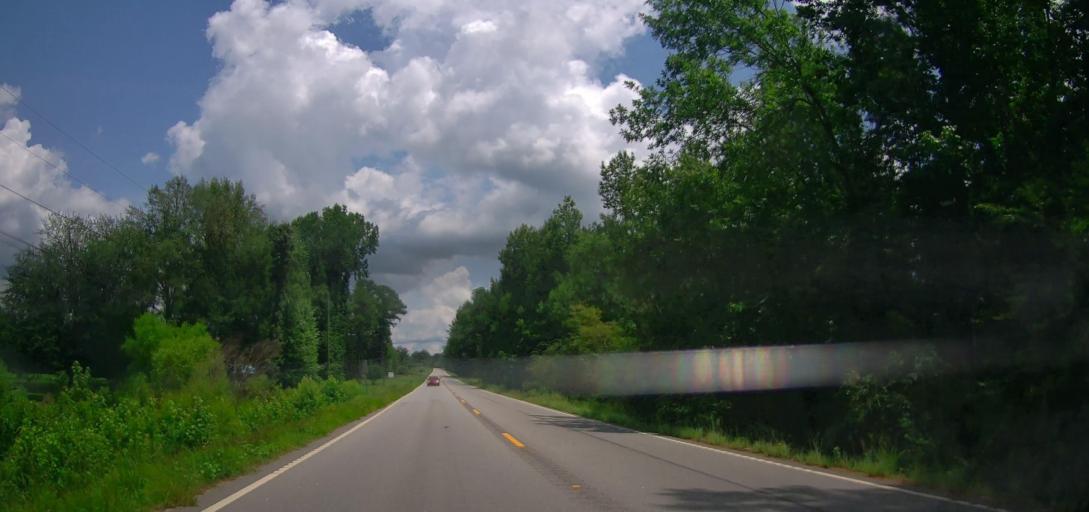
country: US
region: Georgia
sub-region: Meriwether County
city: Greenville
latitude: 33.0101
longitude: -84.6567
